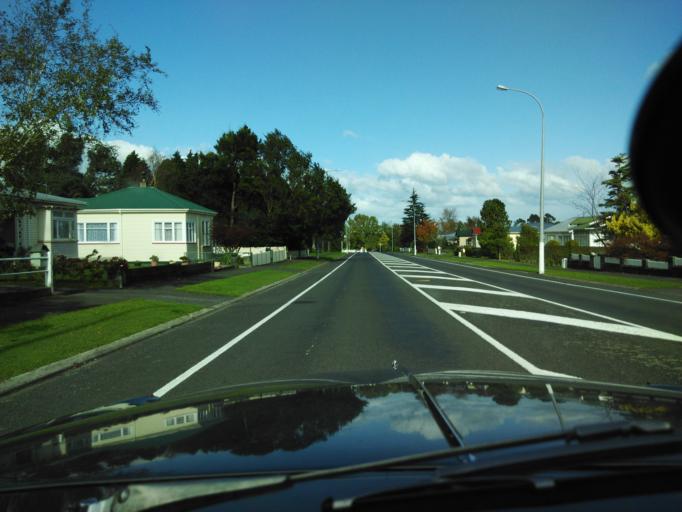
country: NZ
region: Waikato
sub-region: Hauraki District
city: Paeroa
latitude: -37.5350
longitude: 175.7077
